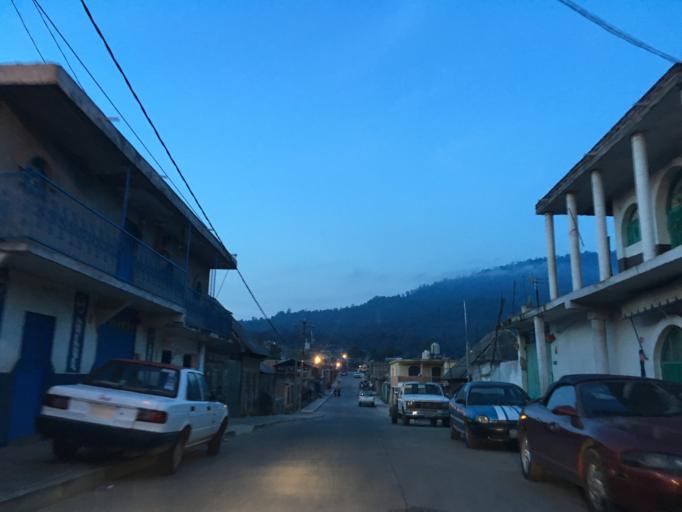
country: MX
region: Michoacan
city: Charapan
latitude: 19.6949
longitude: -102.1898
